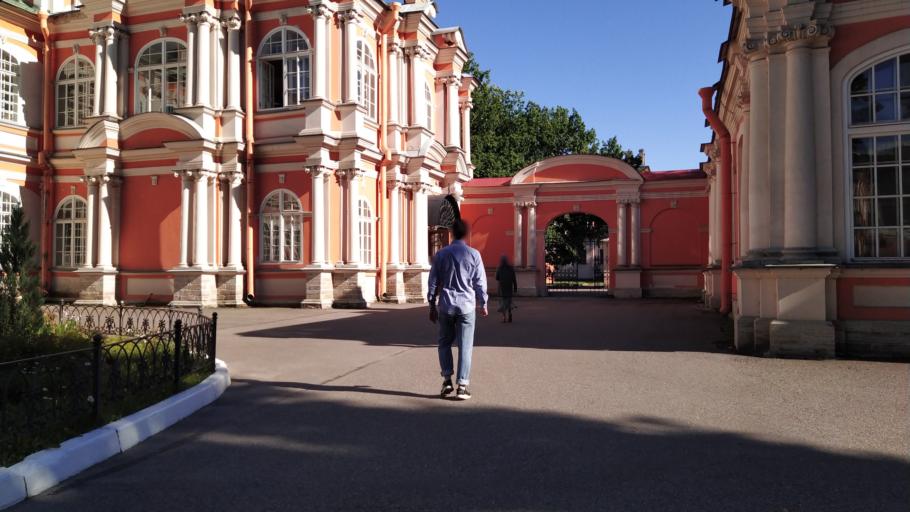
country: RU
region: St.-Petersburg
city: Centralniy
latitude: 59.9202
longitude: 30.3891
